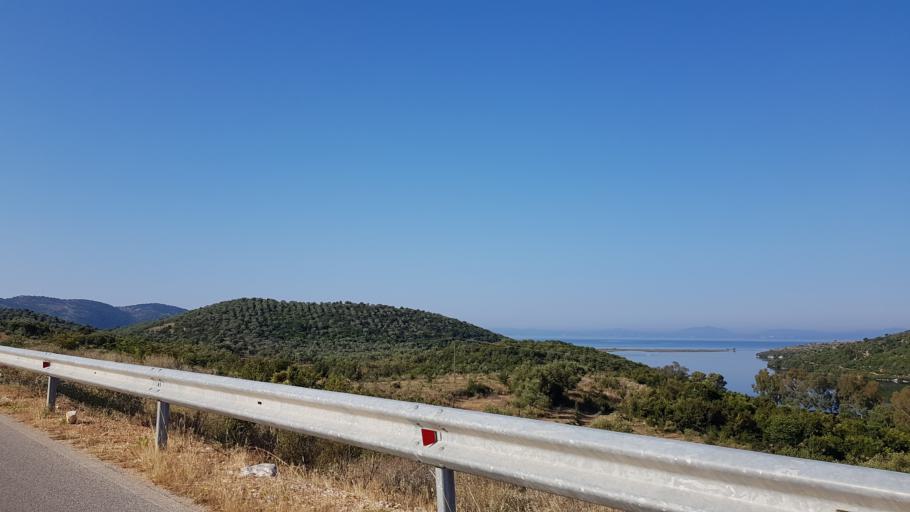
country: AL
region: Vlore
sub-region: Rrethi i Sarandes
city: Xarre
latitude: 39.7550
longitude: 20.0031
